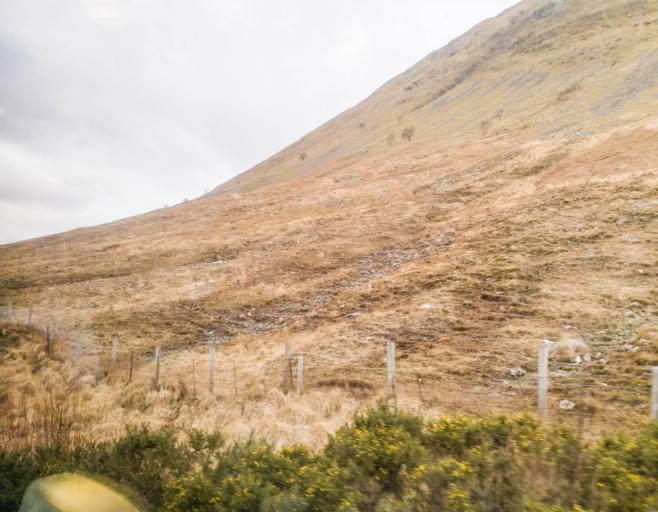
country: GB
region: Scotland
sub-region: Argyll and Bute
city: Garelochhead
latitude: 56.4881
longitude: -4.7235
